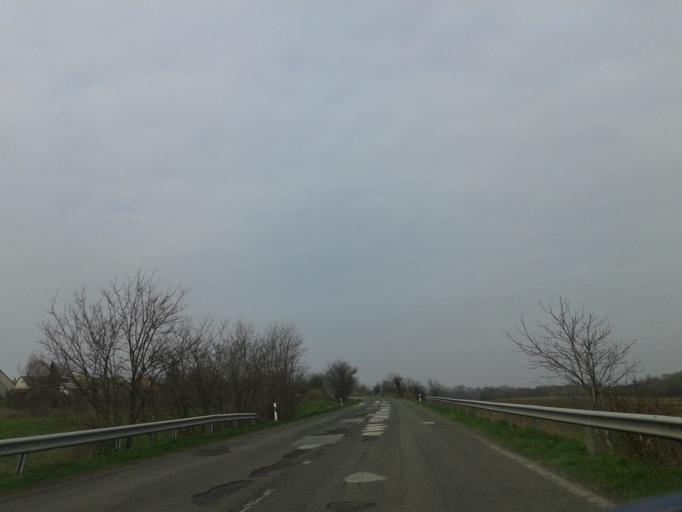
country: HU
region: Komarom-Esztergom
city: Acs
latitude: 47.7254
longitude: 18.0109
